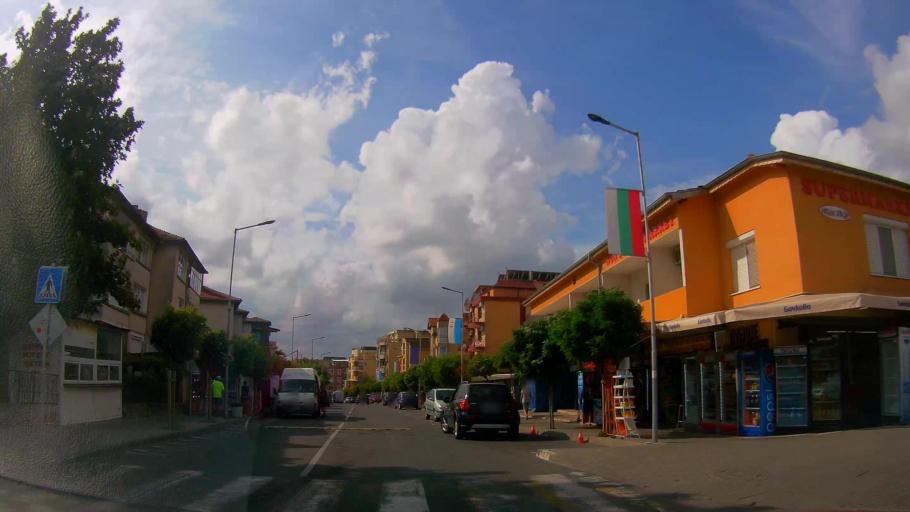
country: BG
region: Burgas
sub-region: Obshtina Primorsko
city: Primorsko
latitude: 42.2684
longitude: 27.7494
